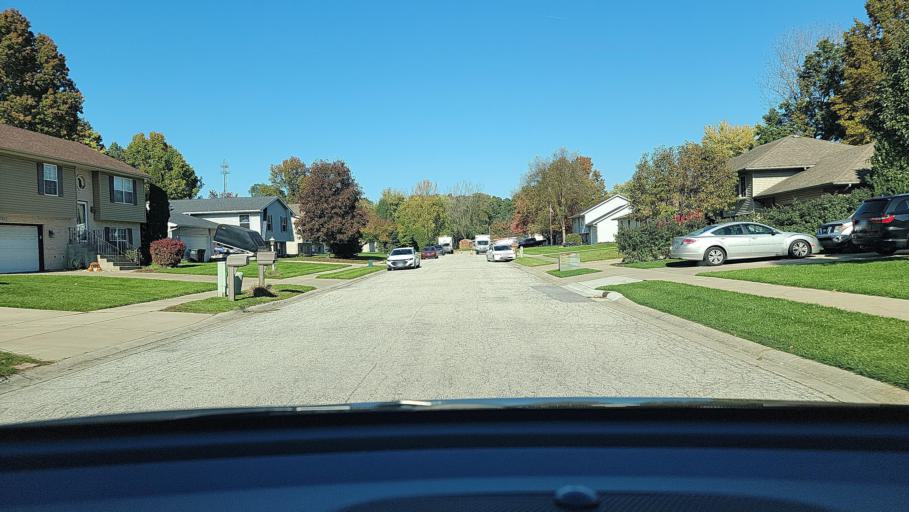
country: US
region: Indiana
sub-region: Porter County
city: Portage
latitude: 41.5808
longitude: -87.1620
